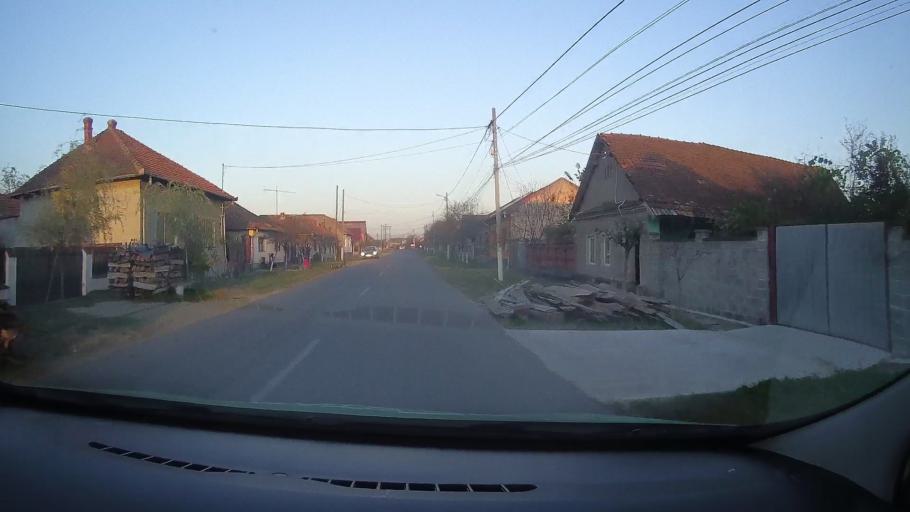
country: RO
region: Timis
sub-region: Comuna Manastiur
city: Manastiur
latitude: 45.8370
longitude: 22.0610
